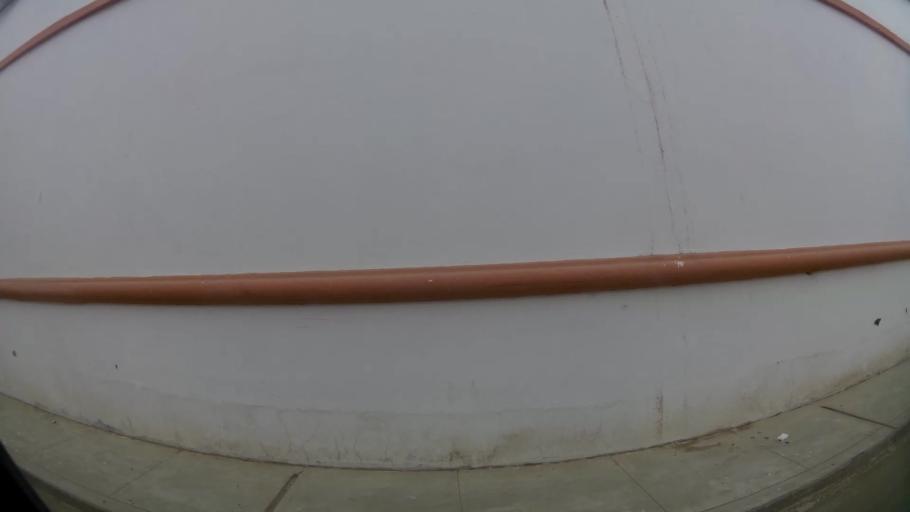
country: PE
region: La Libertad
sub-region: Provincia de Trujillo
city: Trujillo
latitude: -8.1206
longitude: -79.0447
